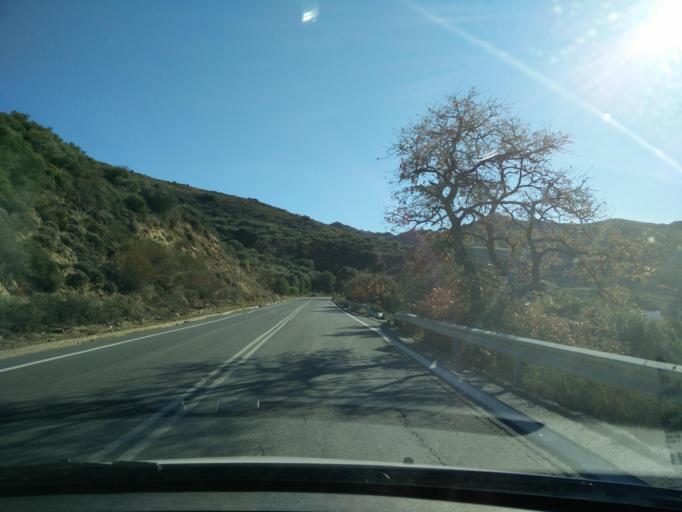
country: GR
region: Crete
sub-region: Nomos Irakleiou
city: Arkalochori
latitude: 35.0758
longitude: 25.3606
